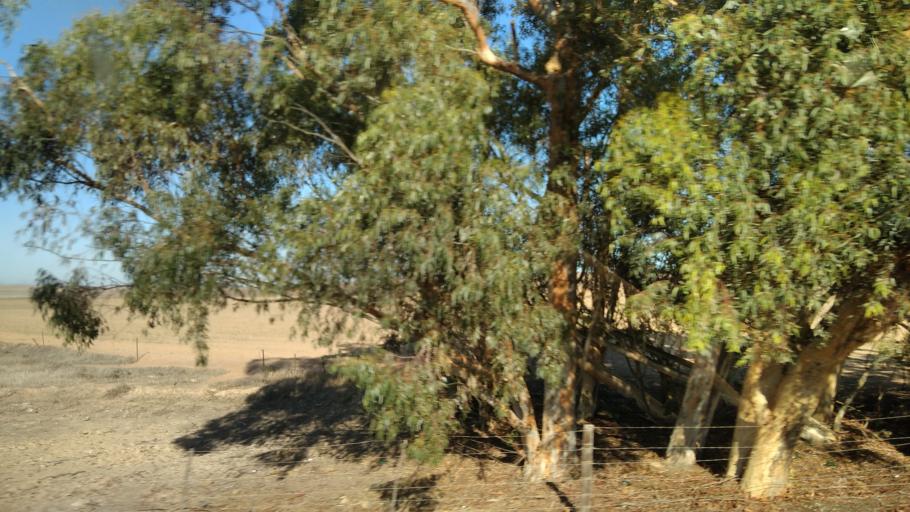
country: ZA
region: Western Cape
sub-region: West Coast District Municipality
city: Moorreesburg
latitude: -33.1456
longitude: 18.4613
